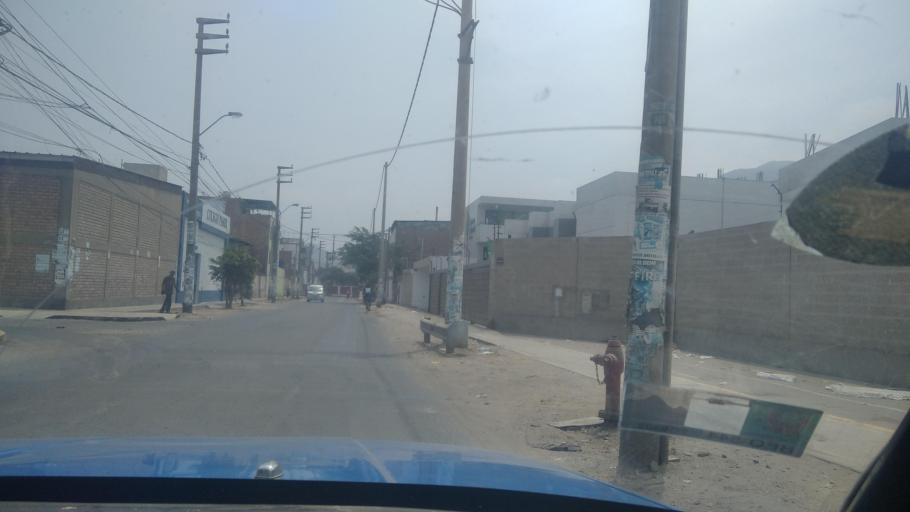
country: PE
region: Lima
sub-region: Lima
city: Independencia
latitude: -11.9815
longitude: -77.0102
